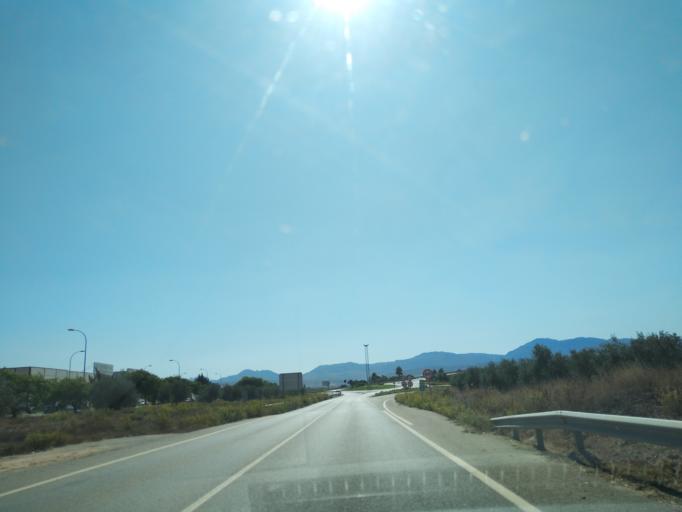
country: ES
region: Andalusia
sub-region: Provincia de Malaga
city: Mollina
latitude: 37.0991
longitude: -4.6340
